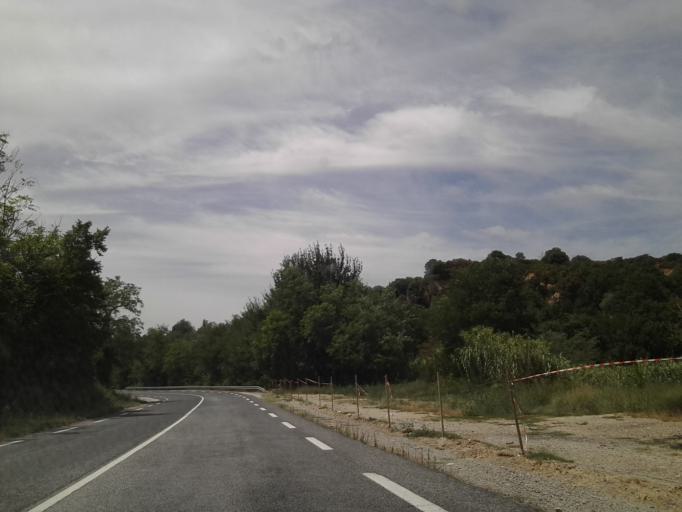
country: FR
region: Languedoc-Roussillon
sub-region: Departement des Pyrenees-Orientales
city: Vinca
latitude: 42.6494
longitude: 2.5704
